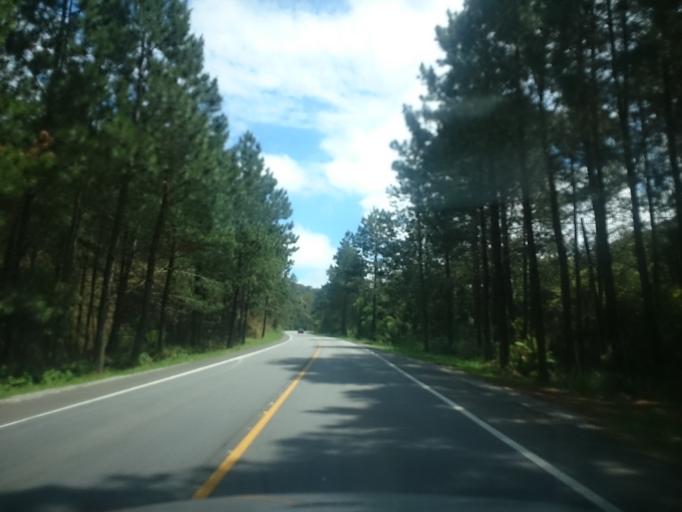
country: BR
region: Santa Catarina
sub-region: Santo Amaro Da Imperatriz
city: Santo Amaro da Imperatriz
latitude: -27.6811
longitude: -49.0225
